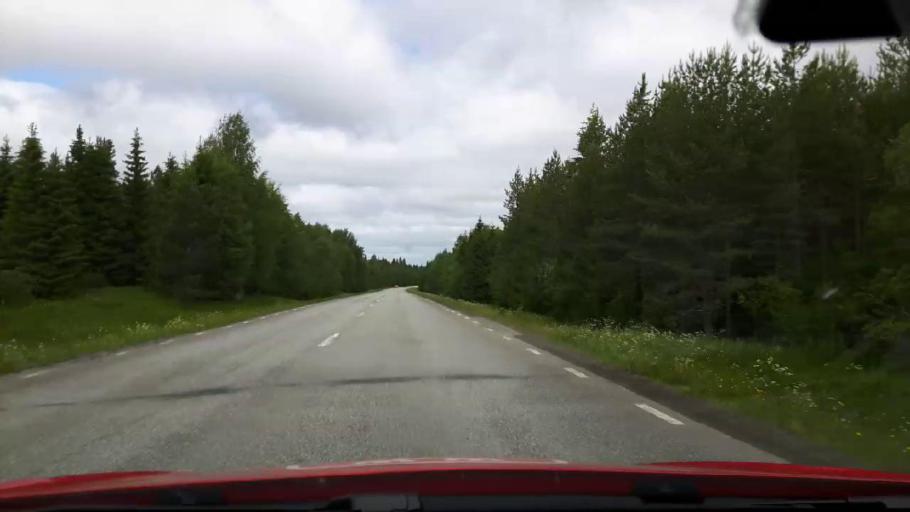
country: SE
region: Jaemtland
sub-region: Krokoms Kommun
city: Krokom
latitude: 63.3718
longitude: 14.5071
